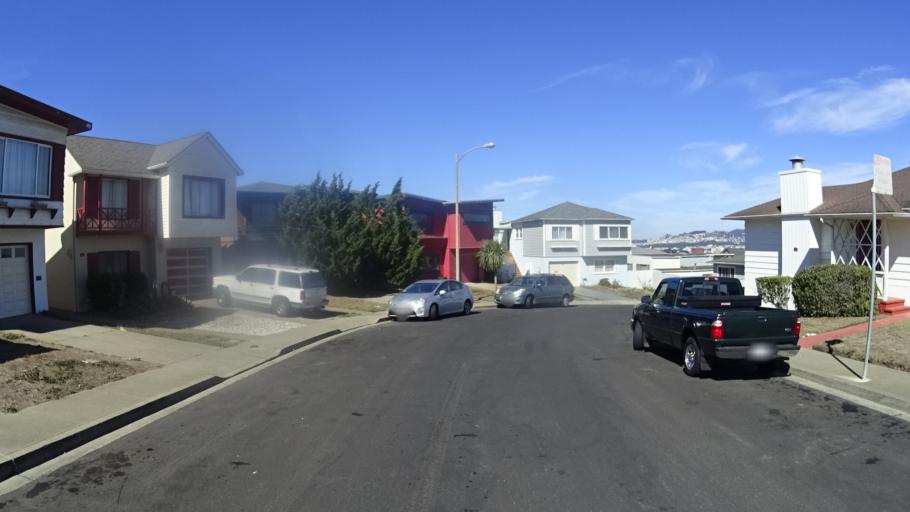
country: US
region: California
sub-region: San Mateo County
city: Broadmoor
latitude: 37.6914
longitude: -122.4955
